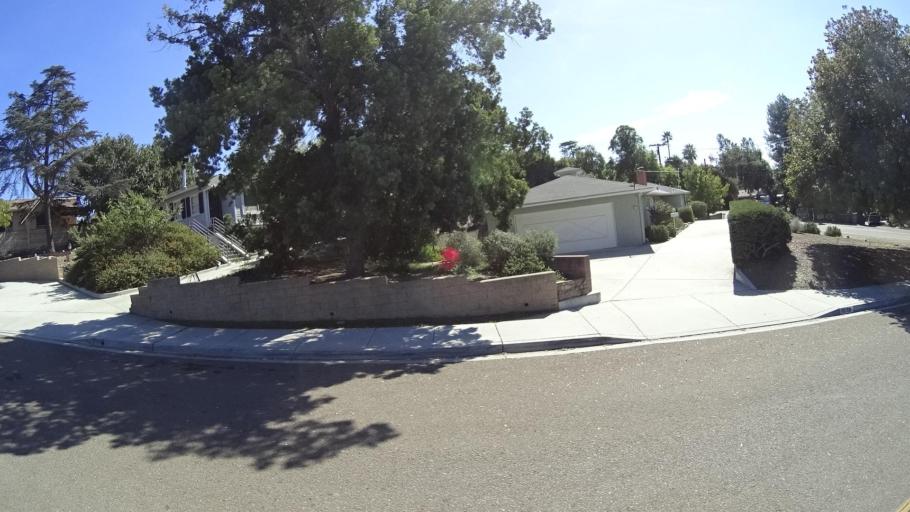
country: US
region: California
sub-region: San Diego County
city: Casa de Oro-Mount Helix
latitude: 32.7476
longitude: -116.9756
